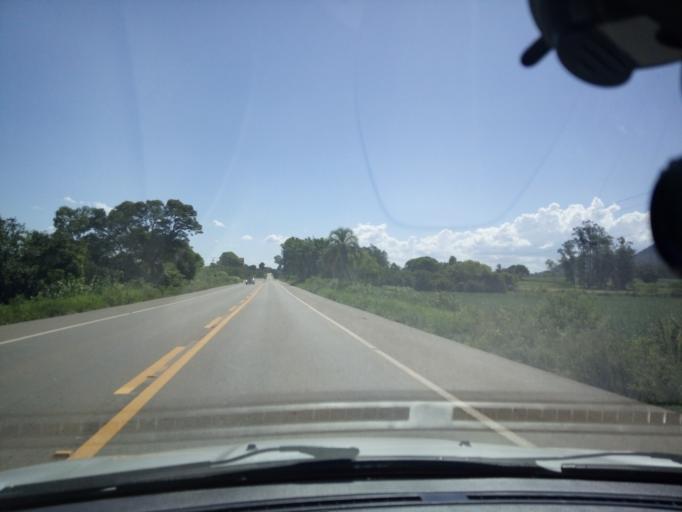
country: BR
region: Rio Grande do Sul
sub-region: Santa Maria
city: Santa Maria
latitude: -29.7330
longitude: -53.5268
